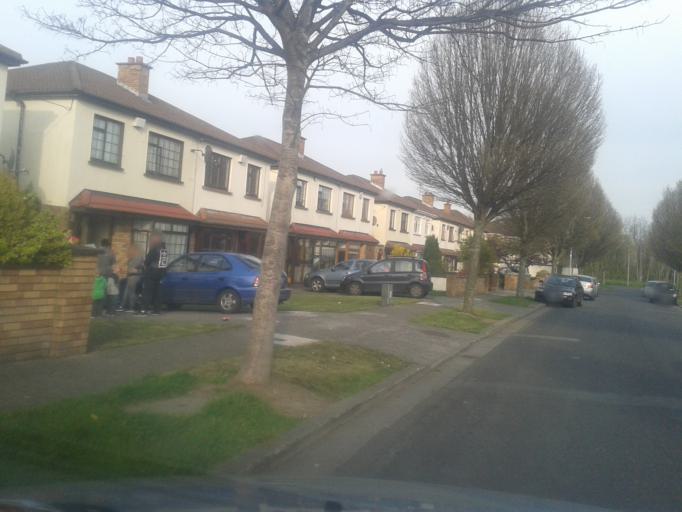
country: IE
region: Leinster
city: Beaumont
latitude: 53.4022
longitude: -6.2381
